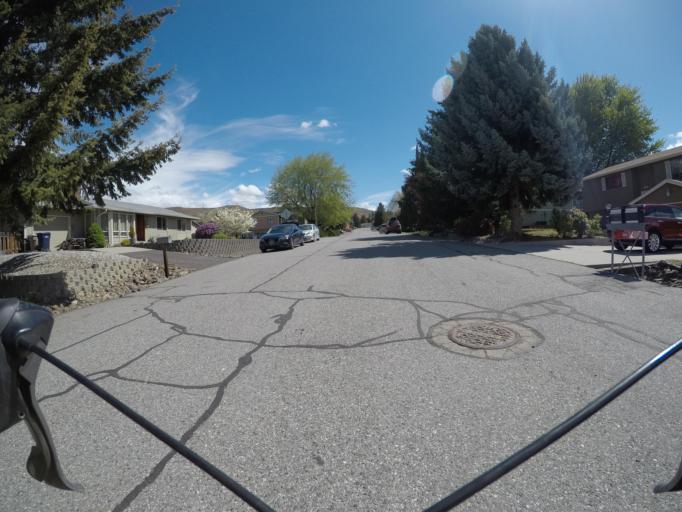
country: US
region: Washington
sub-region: Douglas County
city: East Wenatchee Bench
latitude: 47.4221
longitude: -120.2749
